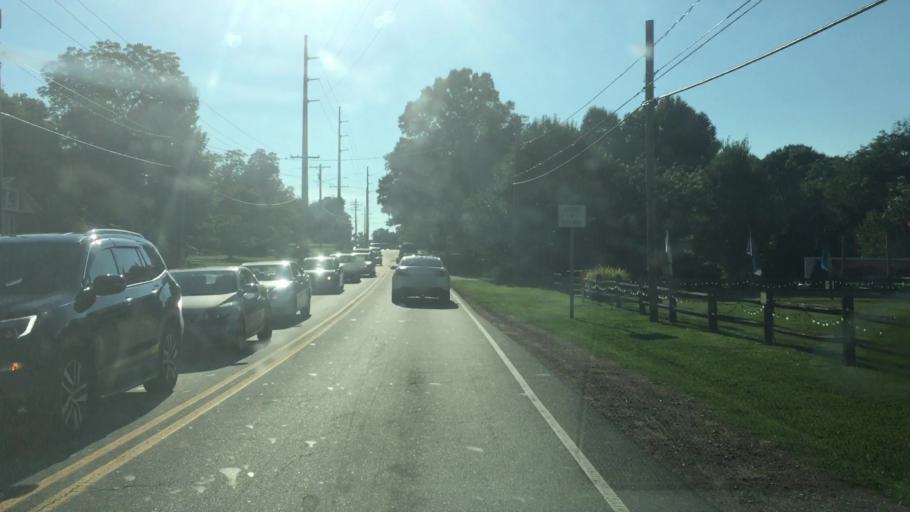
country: US
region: North Carolina
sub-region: Cabarrus County
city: Concord
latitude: 35.4132
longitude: -80.6394
